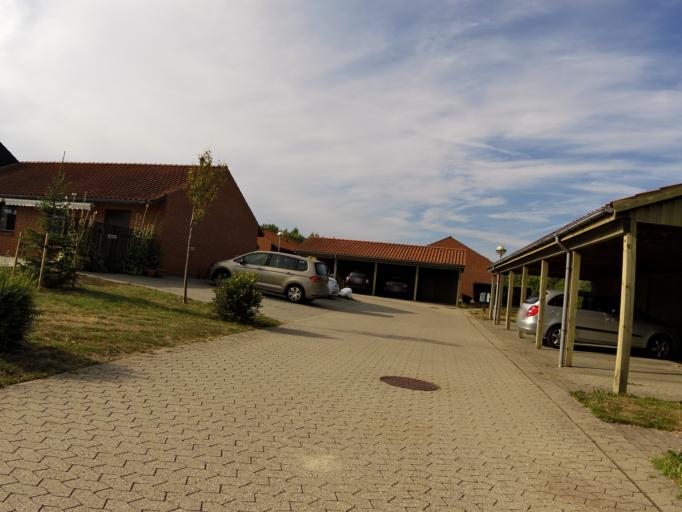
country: DK
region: Capital Region
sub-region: Fredensborg Kommune
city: Niva
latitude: 55.9446
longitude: 12.5070
